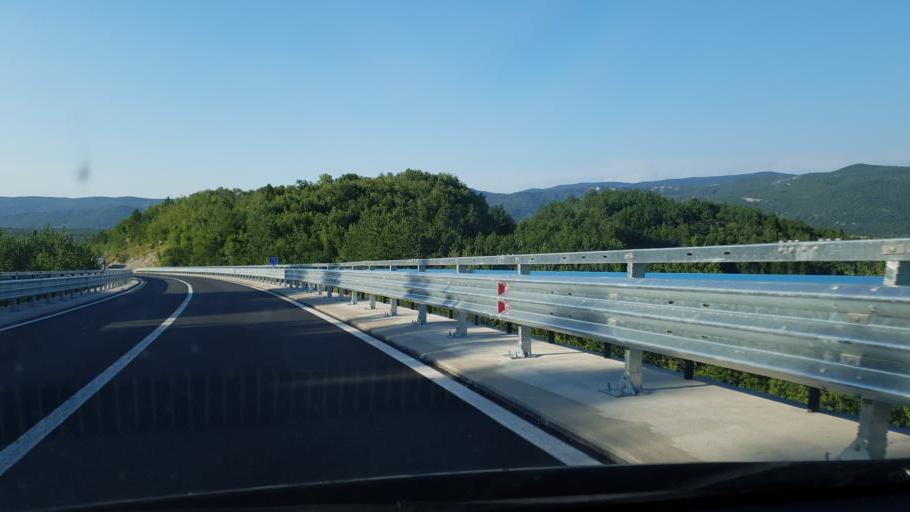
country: HR
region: Istarska
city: Buzet
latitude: 45.3376
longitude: 14.0788
